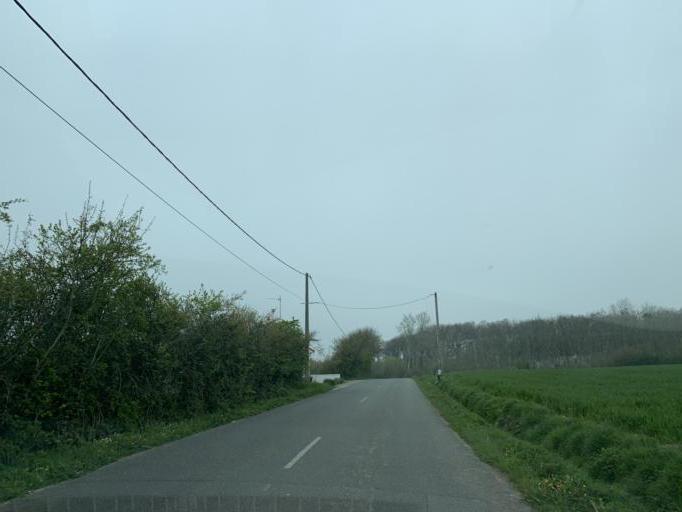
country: FR
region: Nord-Pas-de-Calais
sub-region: Departement du Pas-de-Calais
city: Rety
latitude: 50.7686
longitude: 1.7524
